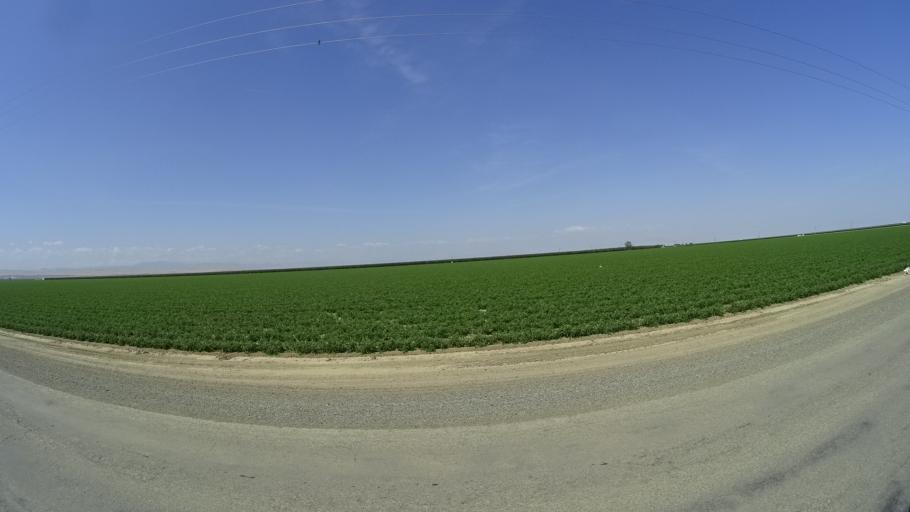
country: US
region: California
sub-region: Fresno County
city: Huron
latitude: 36.1336
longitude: -120.0037
